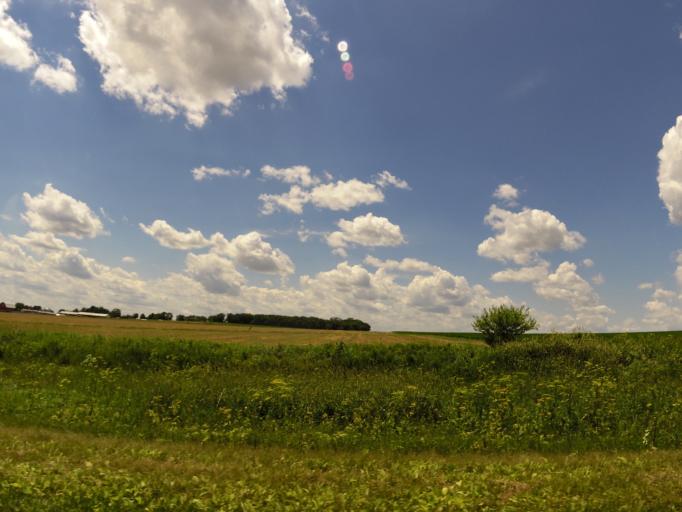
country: US
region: Iowa
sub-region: Buchanan County
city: Independence
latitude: 42.5032
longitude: -91.8896
